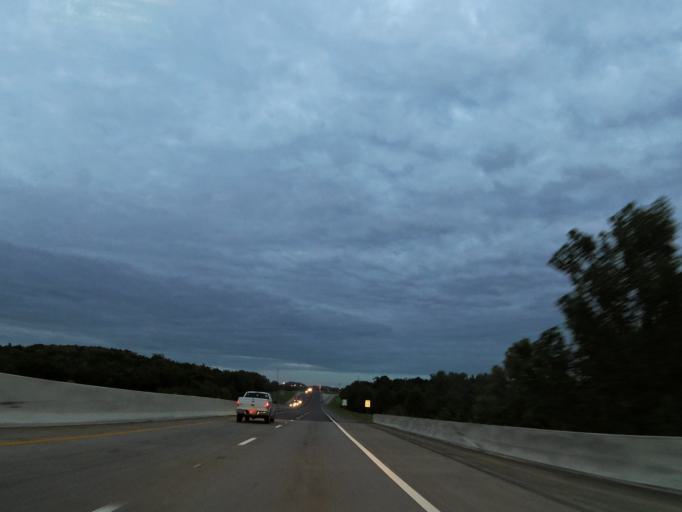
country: US
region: Tennessee
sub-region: Davidson County
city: Nashville
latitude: 36.2328
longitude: -86.8245
